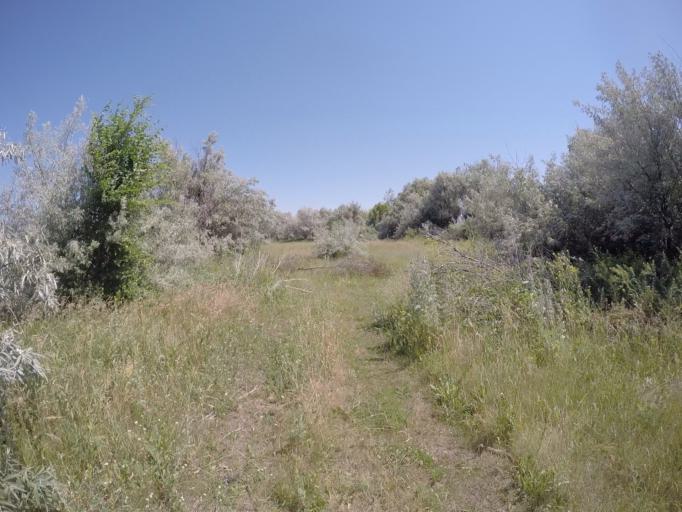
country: RU
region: Saratov
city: Krasnoarmeysk
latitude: 51.1516
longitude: 45.9118
